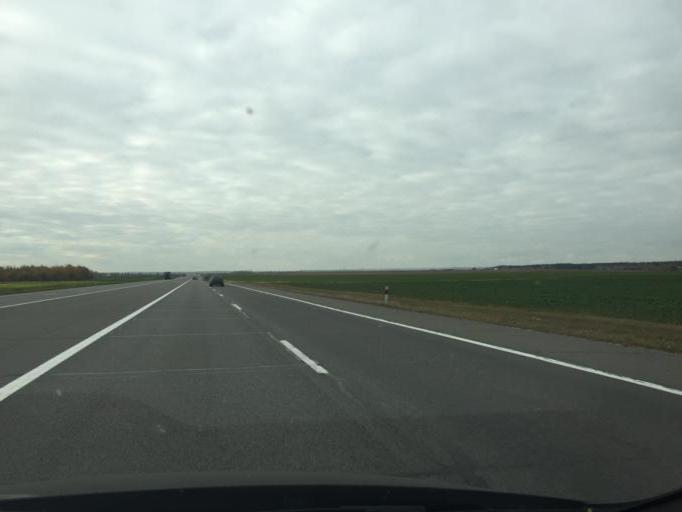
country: BY
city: Fanipol
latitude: 53.6850
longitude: 27.3139
